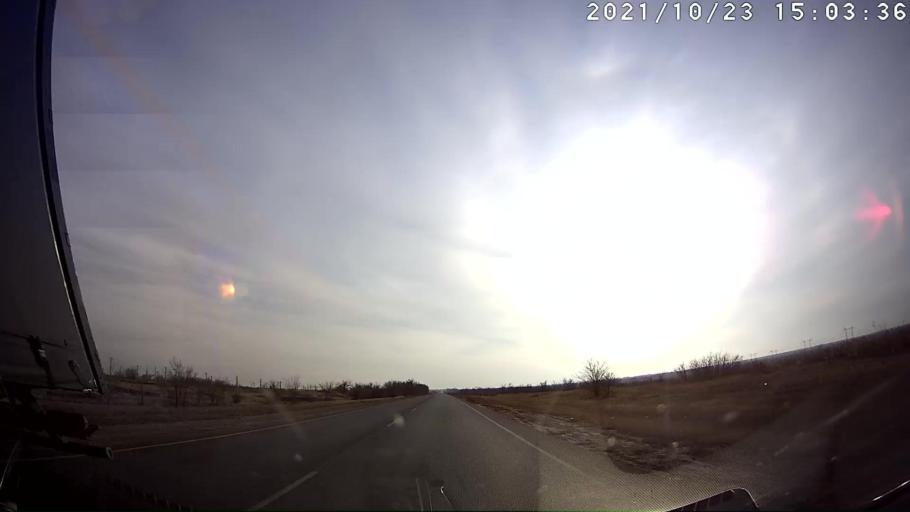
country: RU
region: Volgograd
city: Volgograd
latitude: 48.4106
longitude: 44.3751
